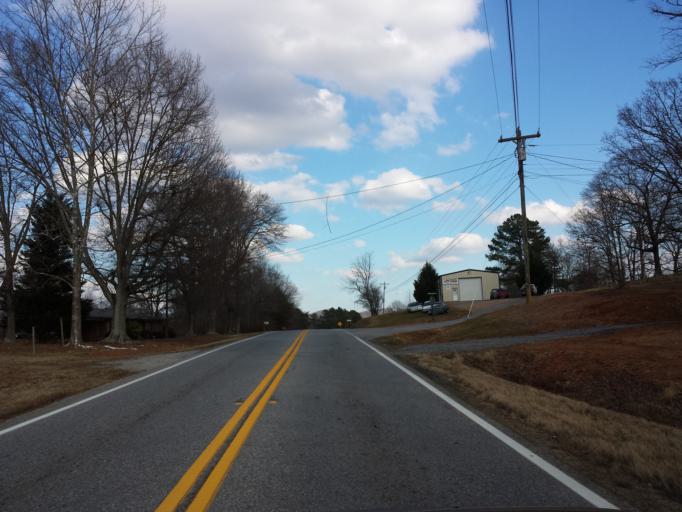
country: US
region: Georgia
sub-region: White County
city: Cleveland
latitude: 34.5420
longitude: -83.8317
